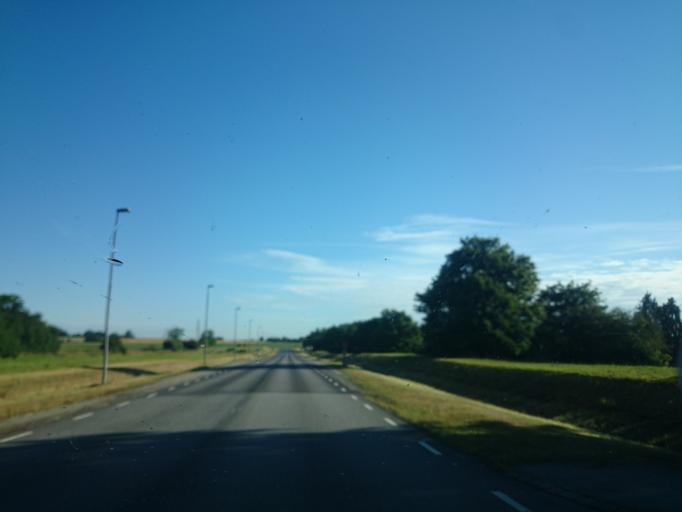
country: SE
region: Skane
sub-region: Eslovs Kommun
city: Eslov
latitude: 55.7190
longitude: 13.3315
